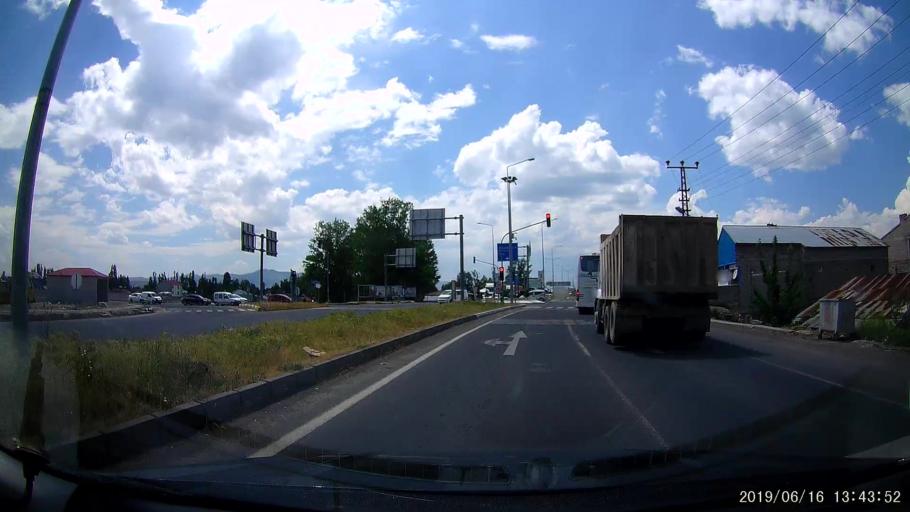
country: TR
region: Agri
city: Agri
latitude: 39.7081
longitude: 43.0496
